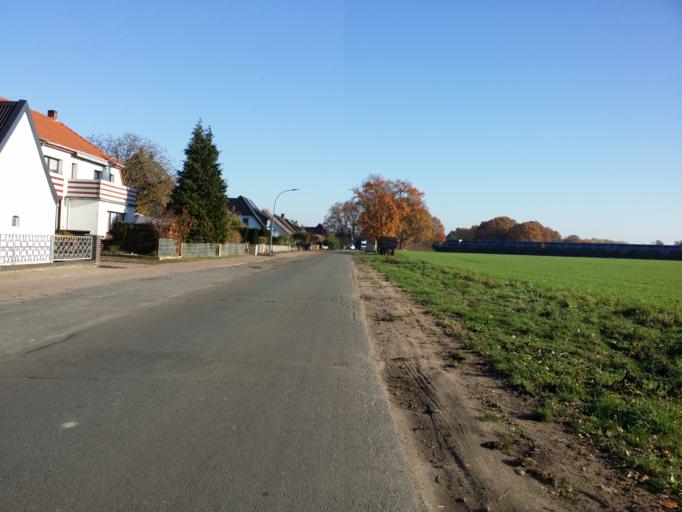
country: DE
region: Lower Saxony
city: Ottersberg
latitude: 53.0621
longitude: 9.0959
